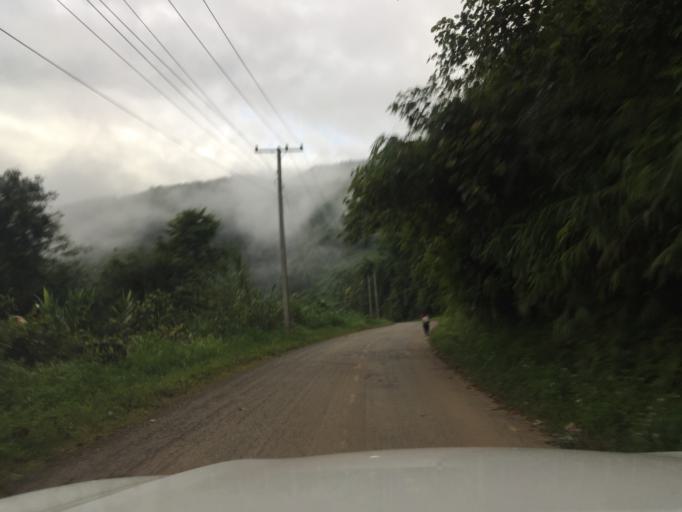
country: LA
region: Phongsali
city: Khoa
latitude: 21.0735
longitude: 102.3760
